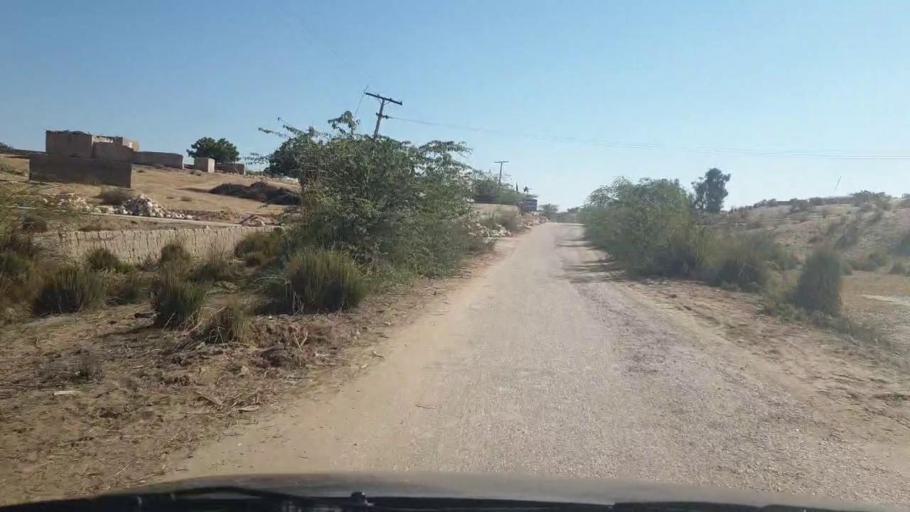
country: PK
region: Sindh
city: Bozdar
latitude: 27.0621
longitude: 68.6270
